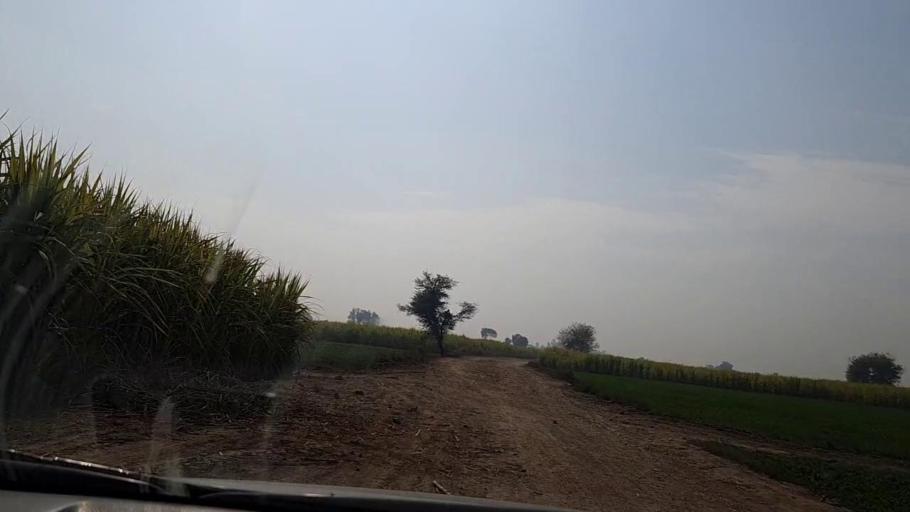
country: PK
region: Sindh
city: Daulatpur
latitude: 26.5389
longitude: 67.9873
